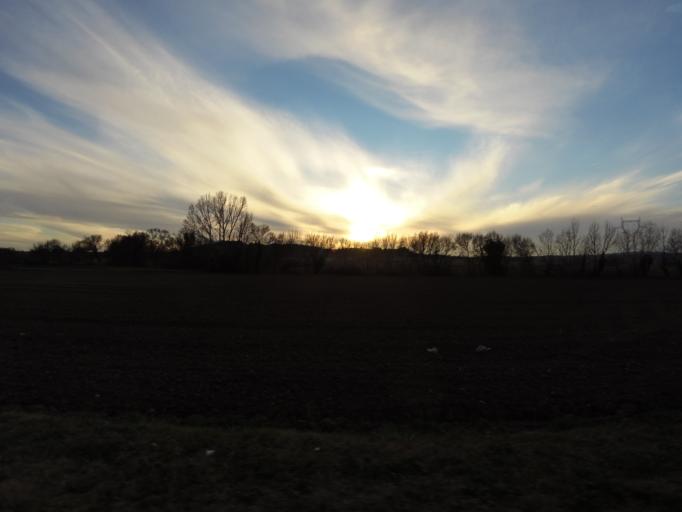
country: FR
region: Languedoc-Roussillon
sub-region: Departement du Gard
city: Saint-Mamert-du-Gard
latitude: 43.8782
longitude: 4.1997
